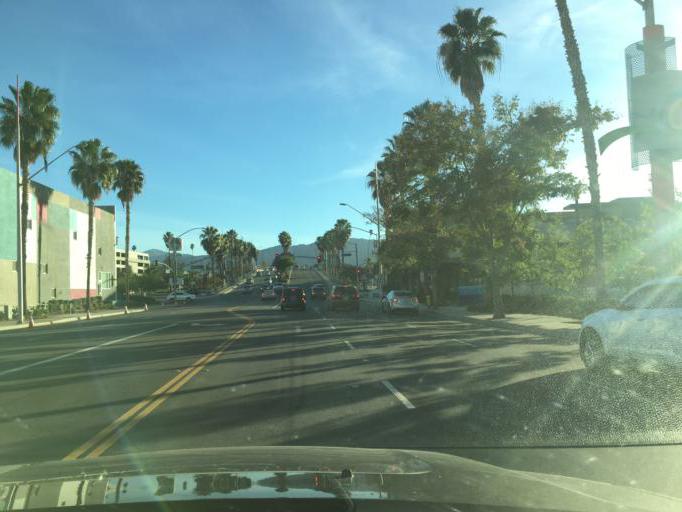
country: US
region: California
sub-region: Riverside County
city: Corona
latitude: 33.8853
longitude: -117.5649
